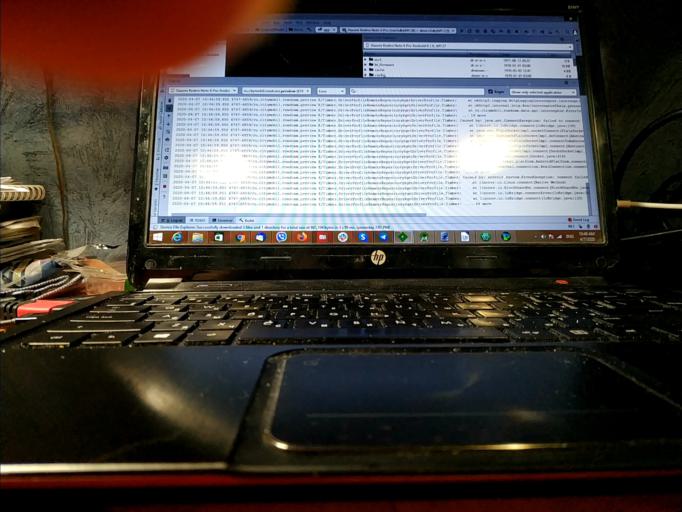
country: RU
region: Vologda
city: Suda
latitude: 58.9225
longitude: 37.5432
